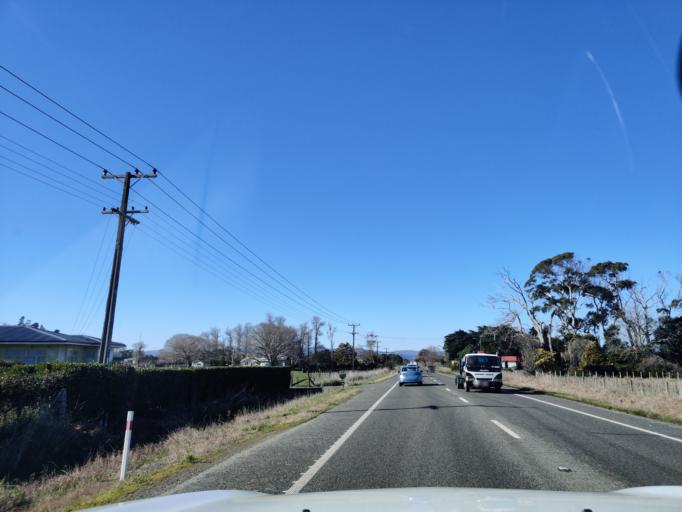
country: NZ
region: Manawatu-Wanganui
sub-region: Palmerston North City
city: Palmerston North
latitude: -40.3039
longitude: 175.5830
